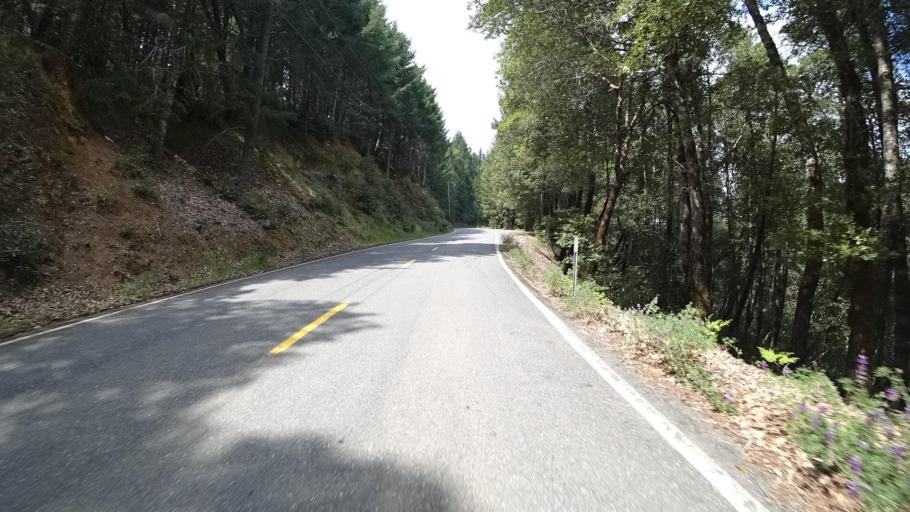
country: US
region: California
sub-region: Humboldt County
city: Redway
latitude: 40.0544
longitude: -123.9896
